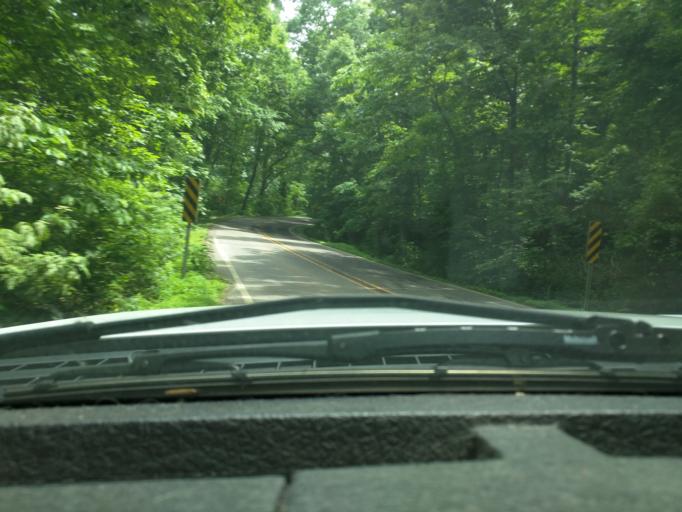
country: US
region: Arkansas
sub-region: Franklin County
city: Ozark
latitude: 35.7220
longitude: -93.8032
